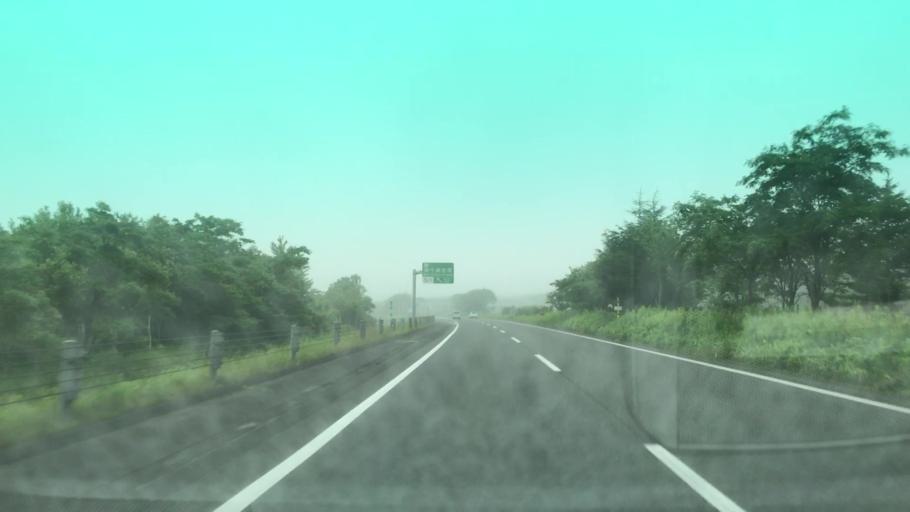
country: JP
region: Hokkaido
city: Chitose
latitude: 42.7807
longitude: 141.6270
